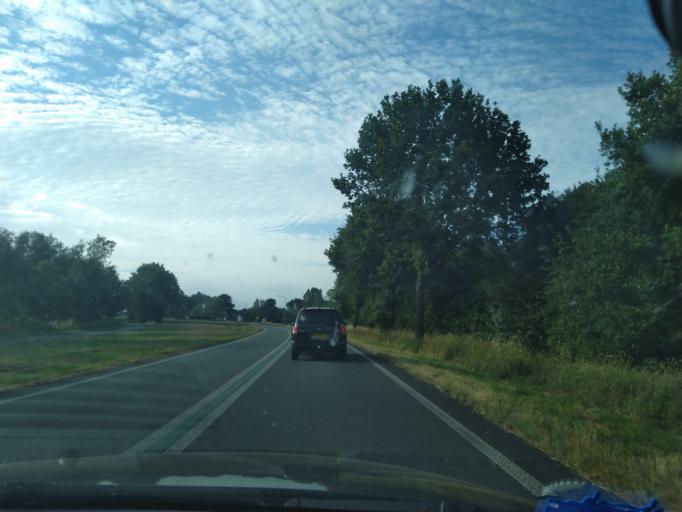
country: NL
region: Groningen
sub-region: Gemeente  Oldambt
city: Winschoten
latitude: 53.1098
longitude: 7.0668
